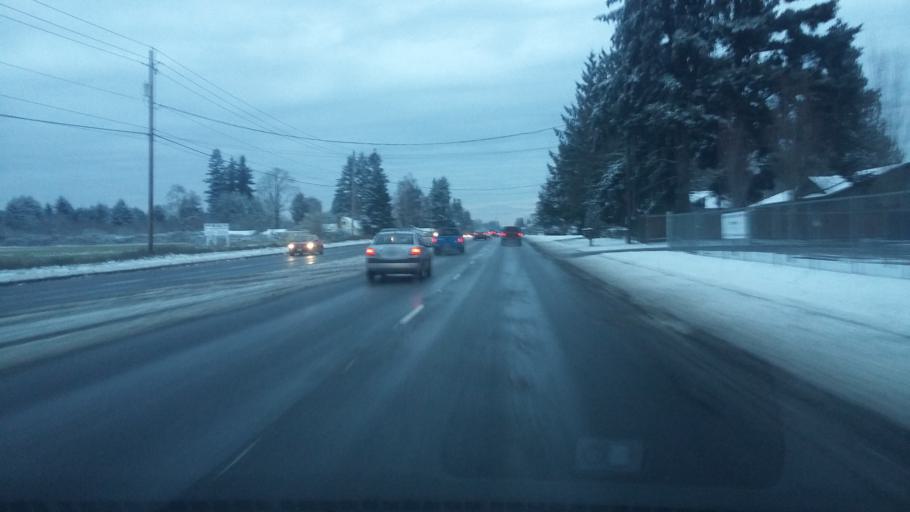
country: US
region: Washington
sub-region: Clark County
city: Brush Prairie
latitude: 45.7130
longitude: -122.5526
